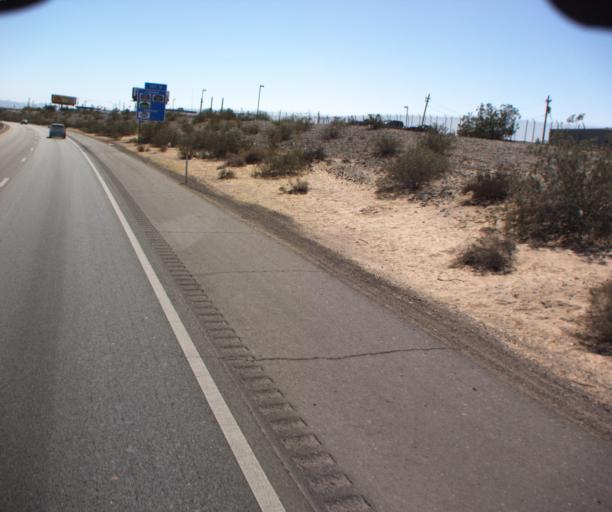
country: US
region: Arizona
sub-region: Yuma County
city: Yuma
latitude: 32.6937
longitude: -114.6030
